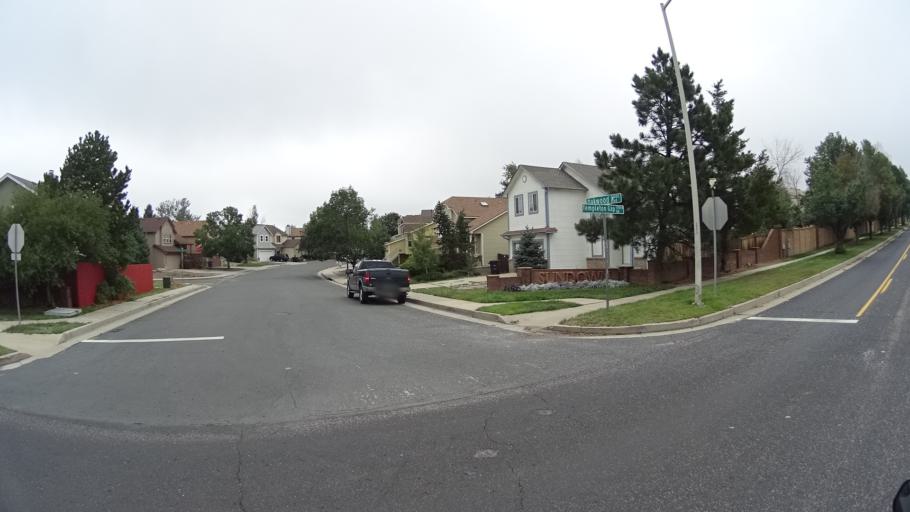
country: US
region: Colorado
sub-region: El Paso County
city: Cimarron Hills
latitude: 38.9195
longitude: -104.7238
